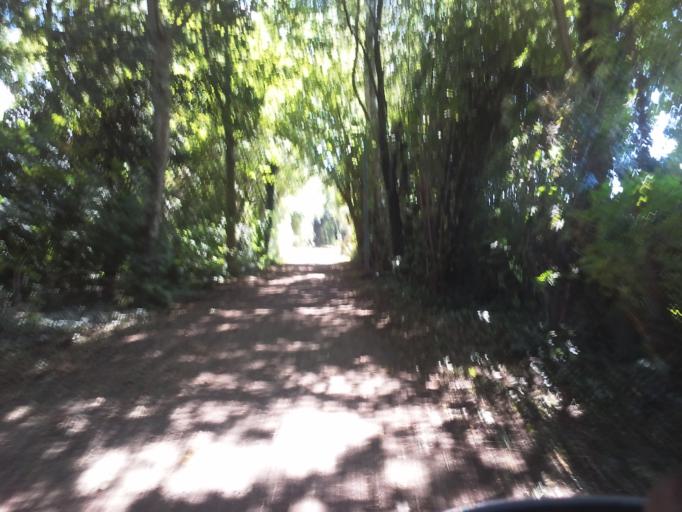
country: DE
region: Lower Saxony
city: Drakenburg
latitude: 52.6723
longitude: 9.2298
